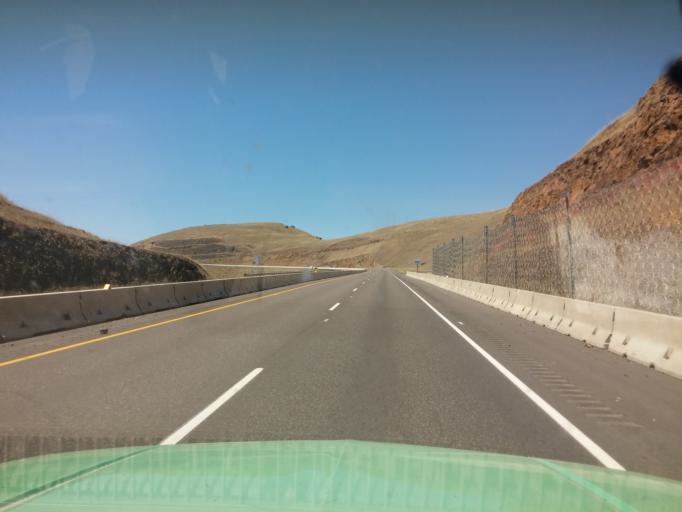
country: US
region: Idaho
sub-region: Nez Perce County
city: Lewiston
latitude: 46.4613
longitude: -116.9791
